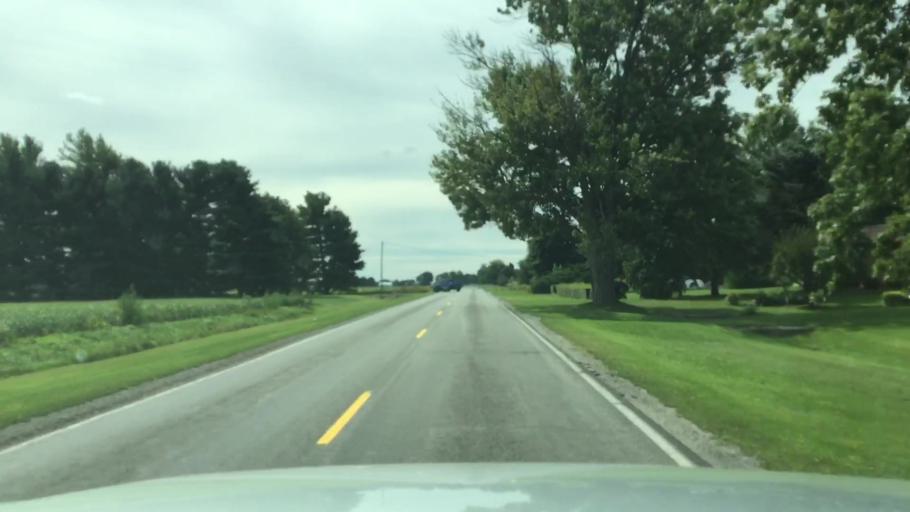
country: US
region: Michigan
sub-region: Genesee County
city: Montrose
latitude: 43.1428
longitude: -83.9883
